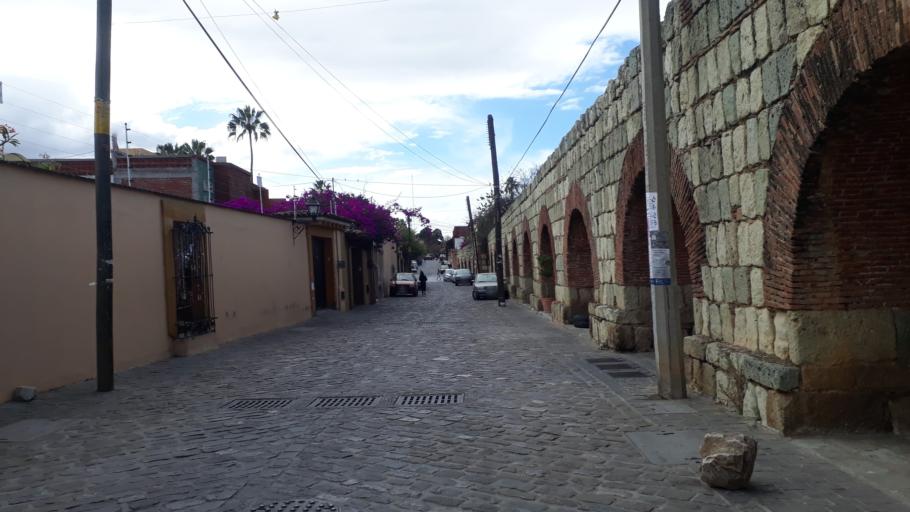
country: MX
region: Oaxaca
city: Oaxaca de Juarez
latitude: 17.0707
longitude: -96.7240
